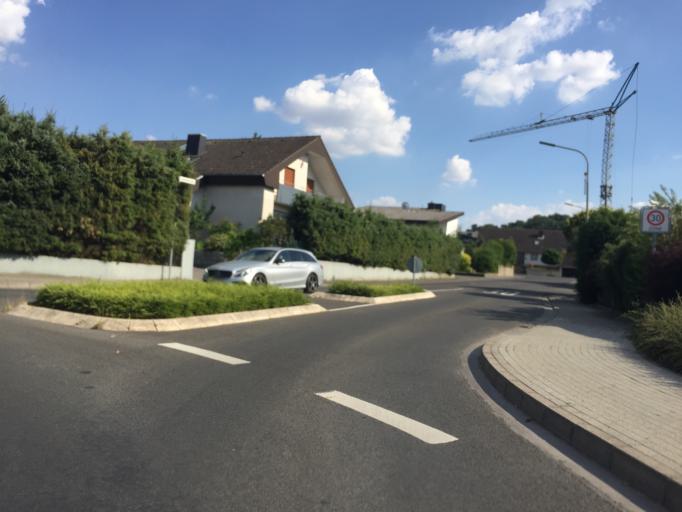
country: DE
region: Hesse
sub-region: Regierungsbezirk Giessen
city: Langgons
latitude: 50.5329
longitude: 8.7034
